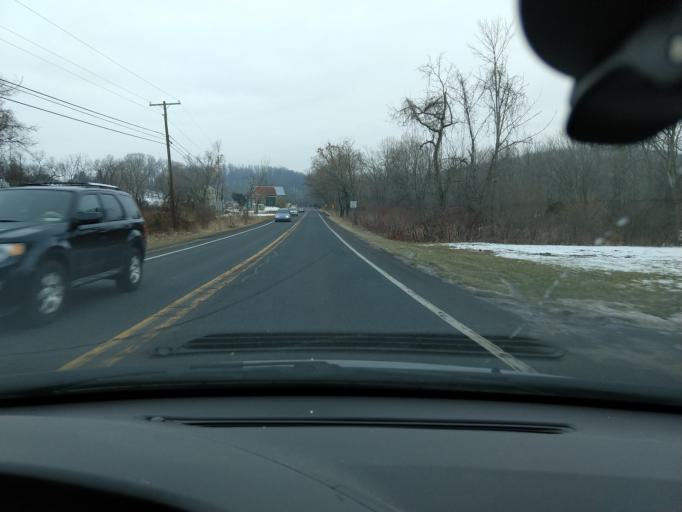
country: US
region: Pennsylvania
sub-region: Lehigh County
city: Macungie
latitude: 40.4665
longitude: -75.5462
